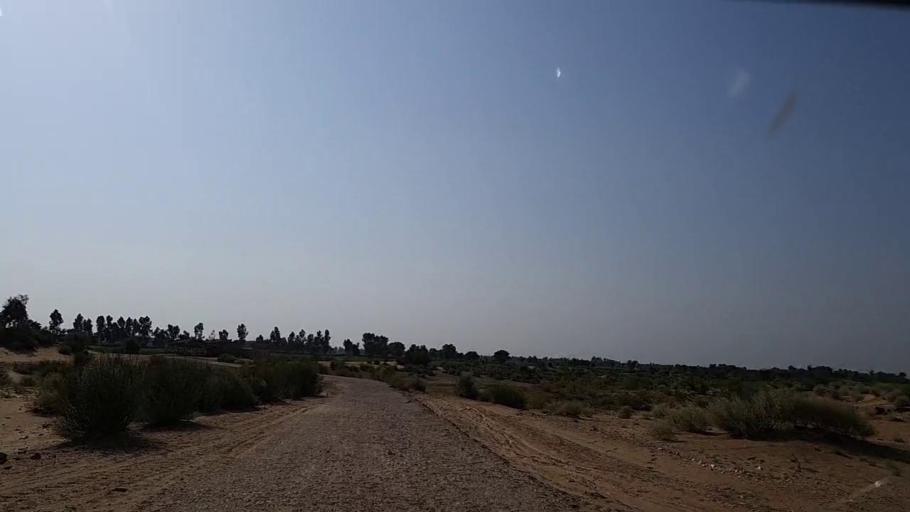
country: PK
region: Sindh
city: Khanpur
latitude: 27.7372
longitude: 69.3721
